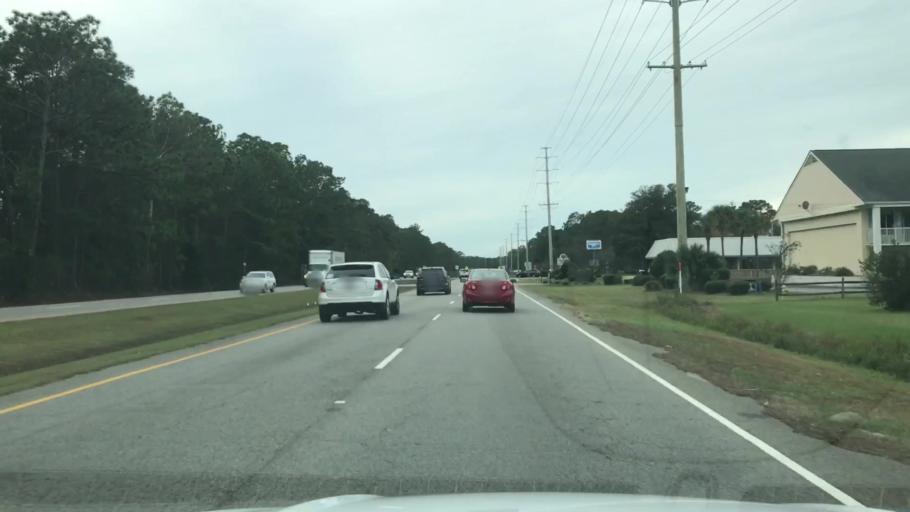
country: US
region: South Carolina
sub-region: Georgetown County
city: Georgetown
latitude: 33.4231
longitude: -79.1666
